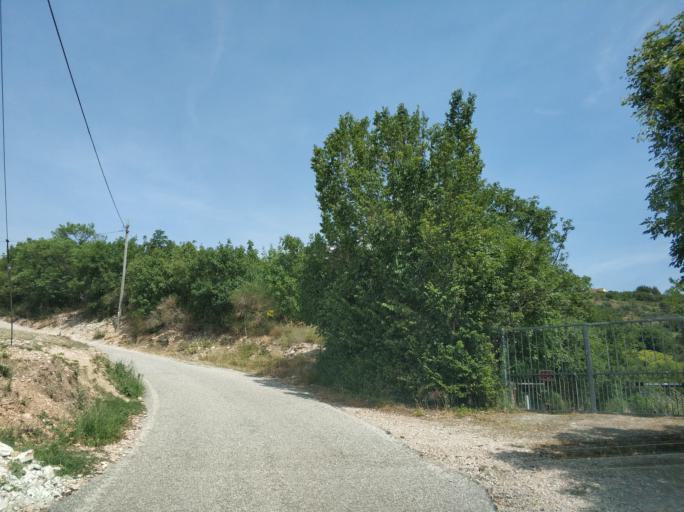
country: IT
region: Veneto
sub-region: Provincia di Padova
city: Arqua Petrarca
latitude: 45.2774
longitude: 11.7072
